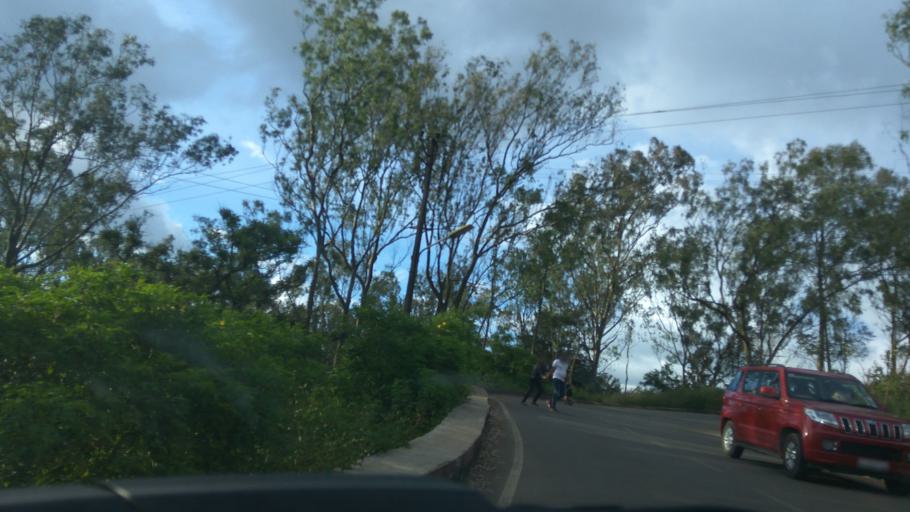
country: IN
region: Karnataka
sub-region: Chikkaballapur
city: Chik Ballapur
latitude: 13.3695
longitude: 77.6810
